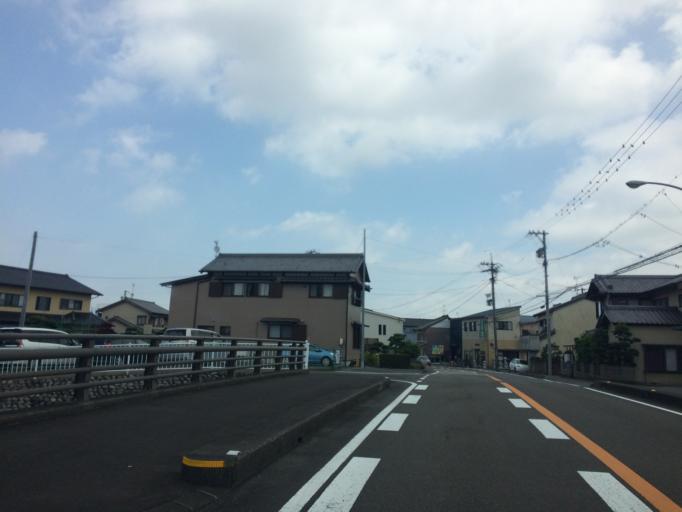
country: JP
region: Shizuoka
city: Fujieda
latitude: 34.8430
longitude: 138.2246
